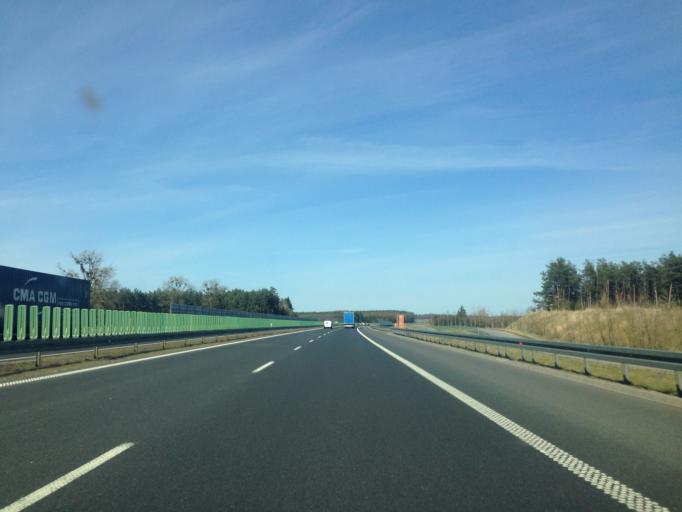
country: PL
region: Pomeranian Voivodeship
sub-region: Powiat starogardzki
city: Smetowo Graniczne
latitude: 53.8034
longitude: 18.6248
